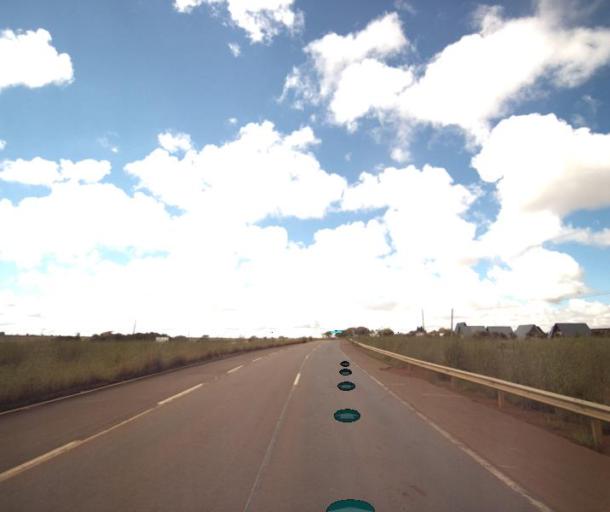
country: BR
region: Goias
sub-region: Anapolis
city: Anapolis
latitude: -16.2500
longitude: -48.9970
